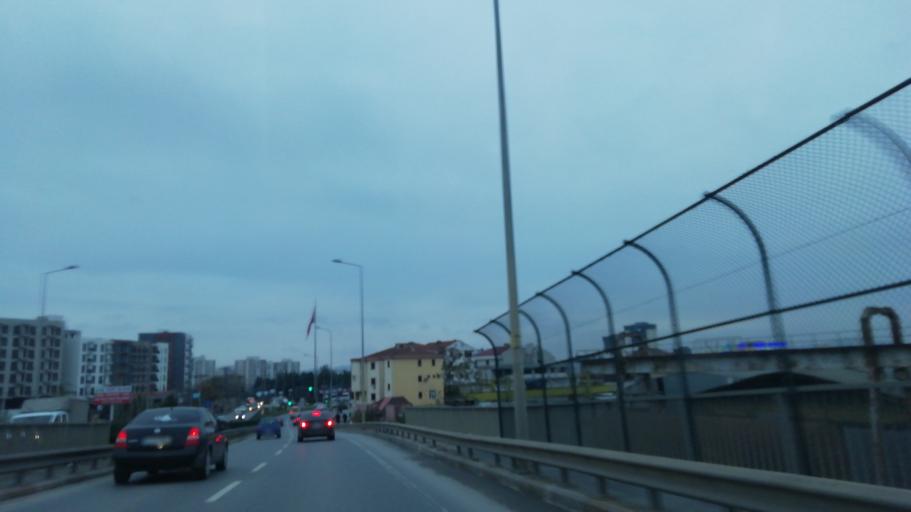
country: TR
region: Istanbul
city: Samandira
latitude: 40.9761
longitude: 29.2389
